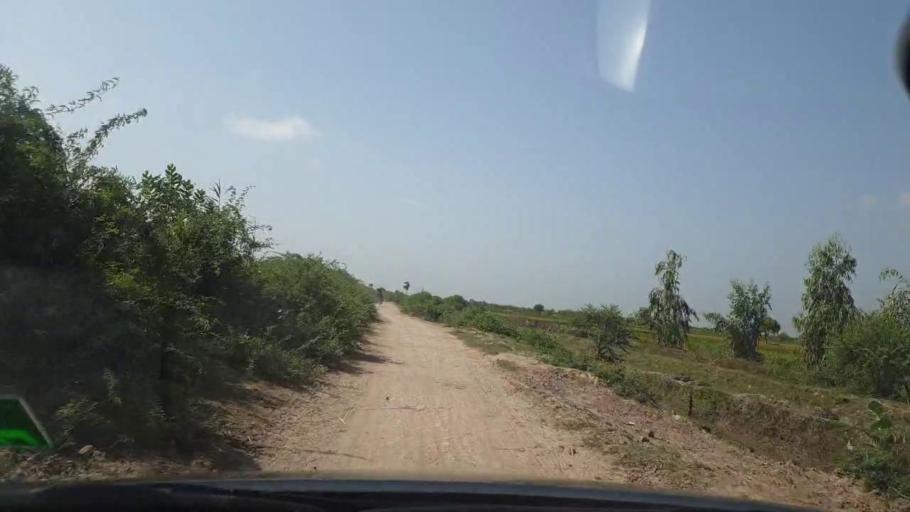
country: PK
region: Sindh
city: Tando Bago
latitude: 24.7662
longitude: 68.9438
